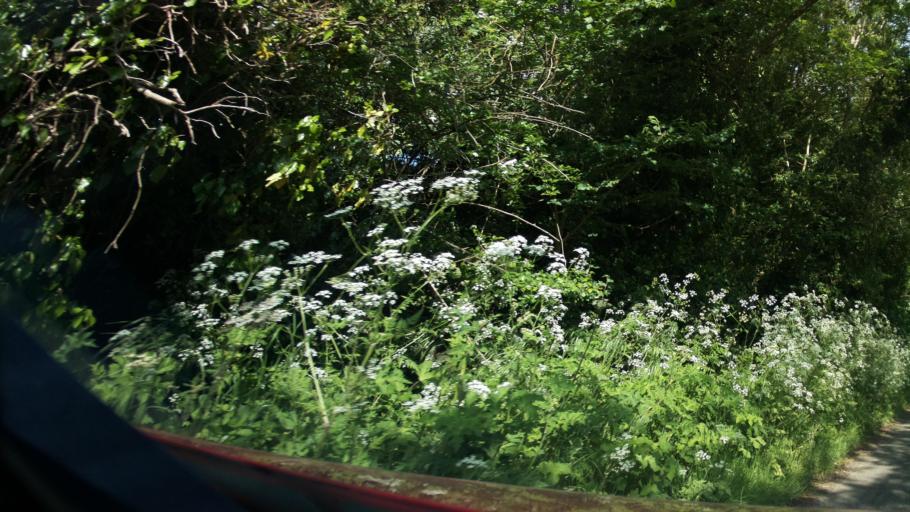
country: GB
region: England
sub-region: Wiltshire
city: Luckington
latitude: 51.5778
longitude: -2.2197
